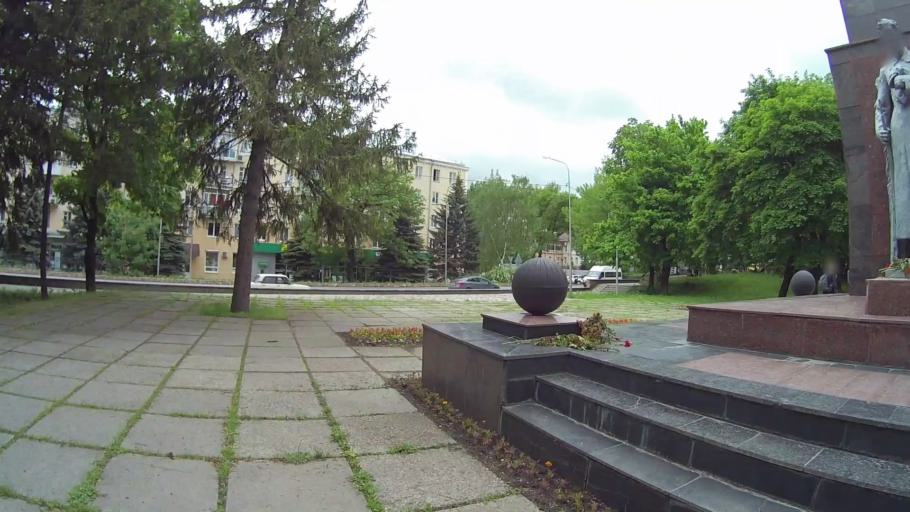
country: RU
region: Stavropol'skiy
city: Zheleznovodsk
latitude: 44.1320
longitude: 43.0290
